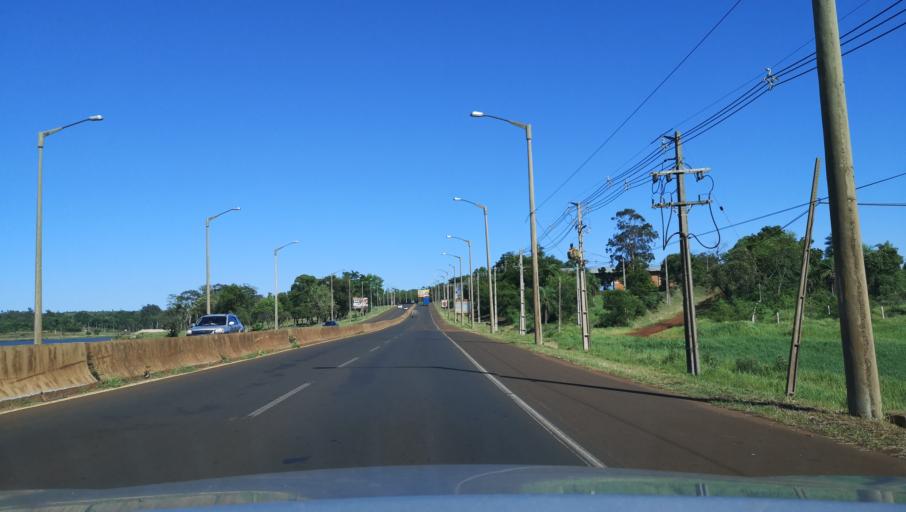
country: PY
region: Itapua
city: San Juan del Parana
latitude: -27.2949
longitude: -55.9112
